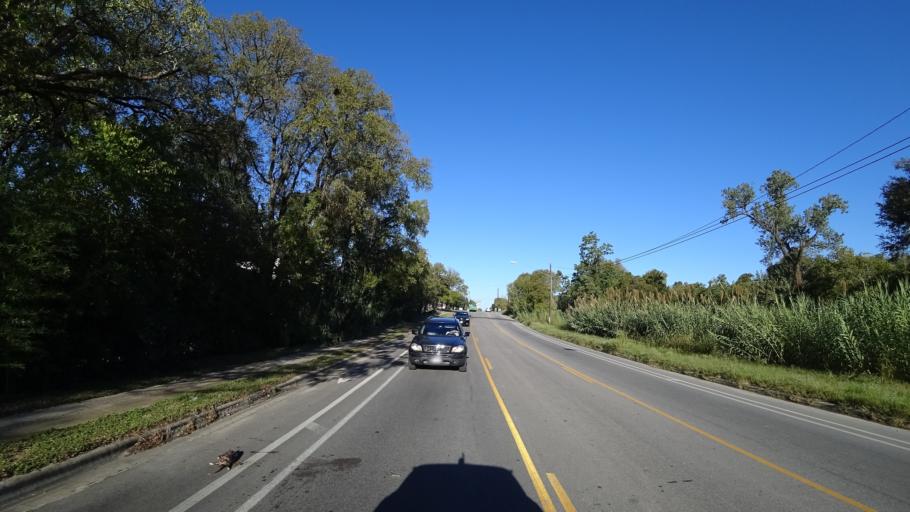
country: US
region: Texas
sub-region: Travis County
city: Austin
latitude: 30.2948
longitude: -97.6803
